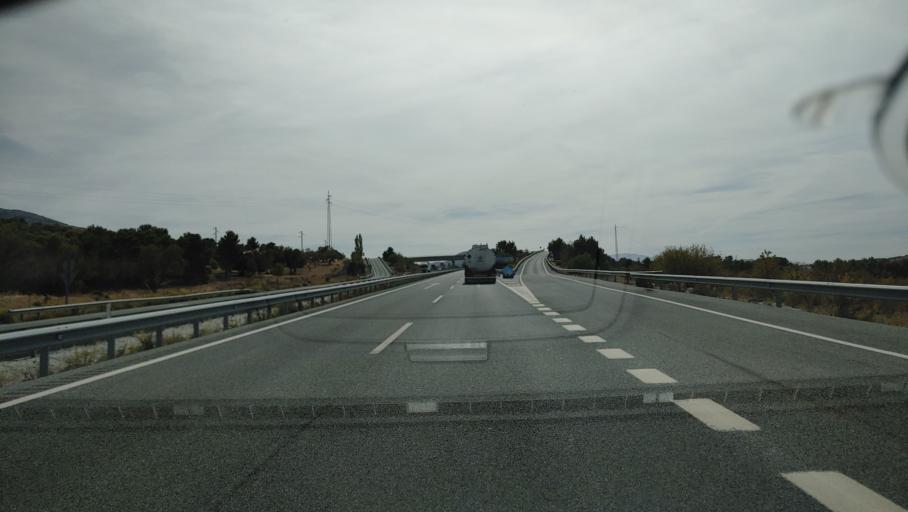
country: ES
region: Andalusia
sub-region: Provincia de Granada
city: Gor
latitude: 37.4255
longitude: -2.9141
